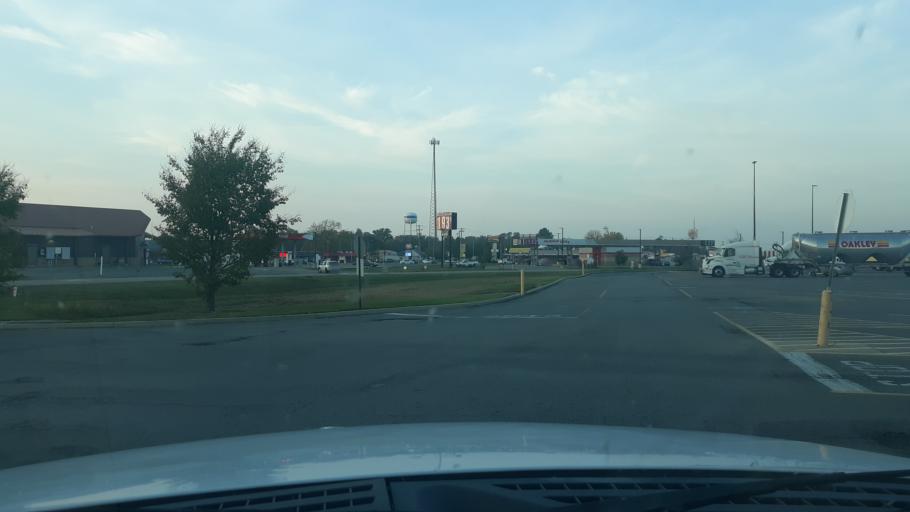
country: US
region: Illinois
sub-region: Saline County
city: Harrisburg
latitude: 37.7280
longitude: -88.5351
